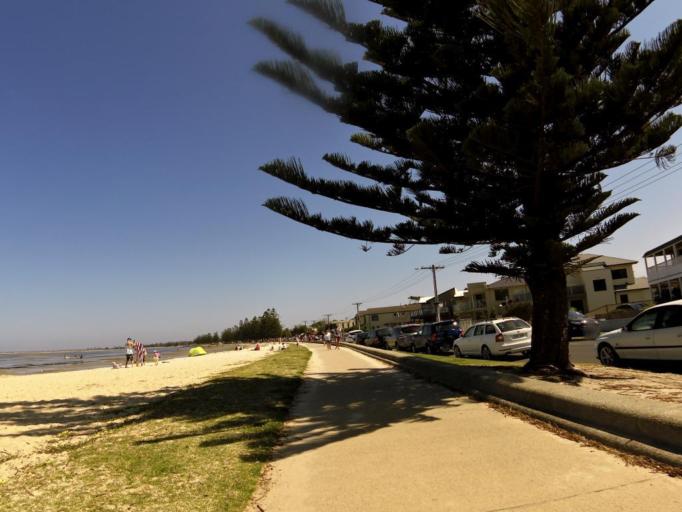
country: AU
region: Victoria
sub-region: Hobsons Bay
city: Altona
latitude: -37.8711
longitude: 144.8241
